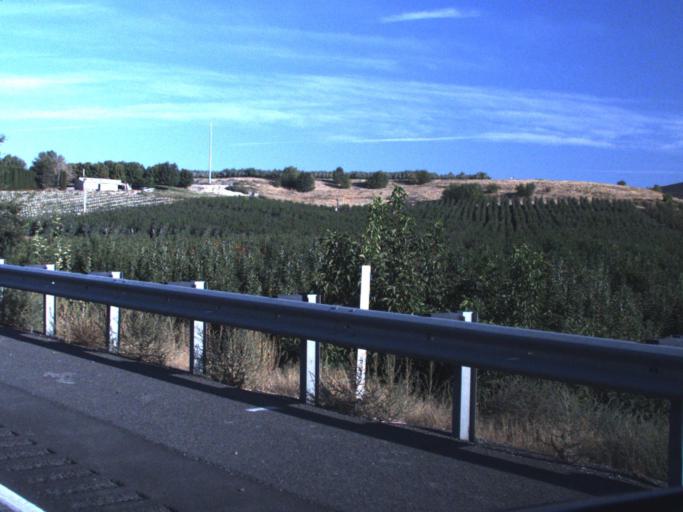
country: US
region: Washington
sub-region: Yakima County
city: Wapato
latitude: 46.4987
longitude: -120.4409
